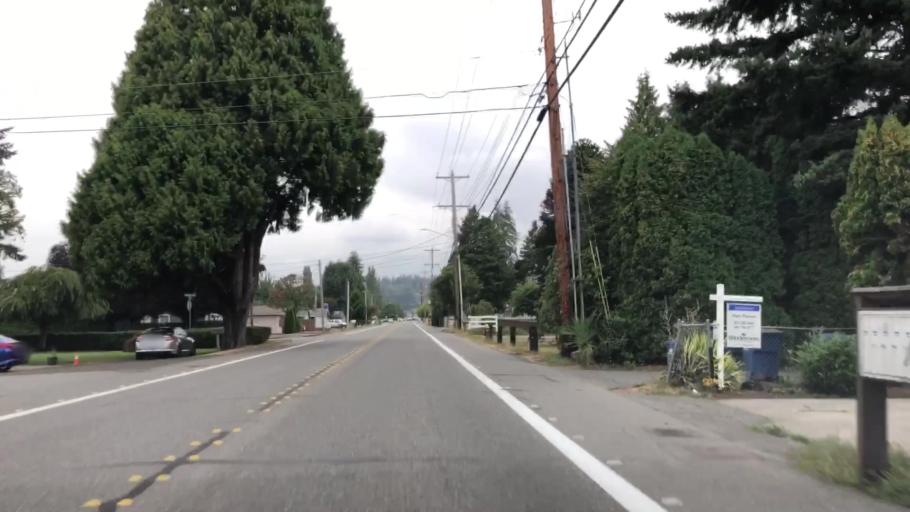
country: US
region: Washington
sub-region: Snohomish County
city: Monroe
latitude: 47.8593
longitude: -121.9906
